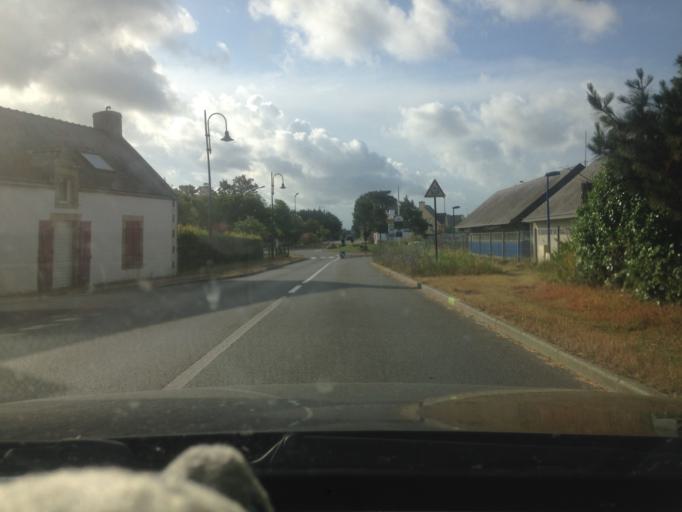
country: FR
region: Brittany
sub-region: Departement du Morbihan
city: Carnac
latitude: 47.5886
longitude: -3.0914
